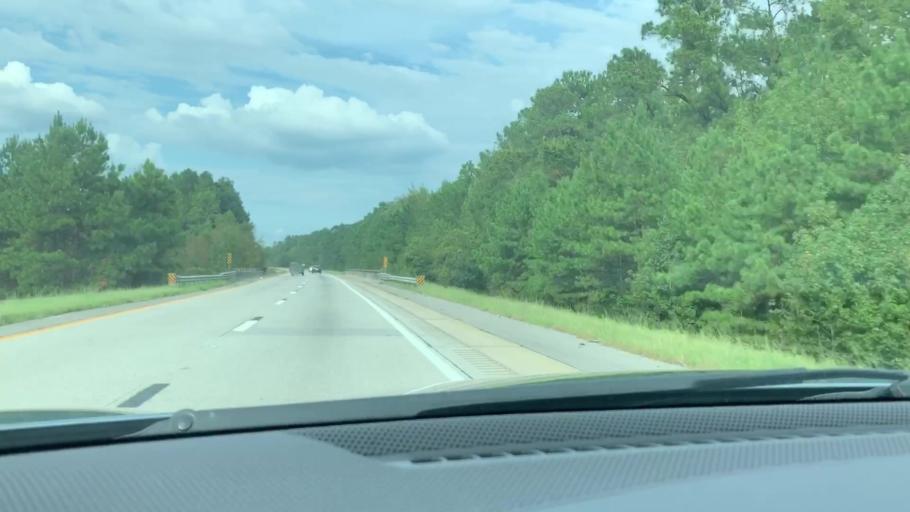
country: US
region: South Carolina
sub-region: Dorchester County
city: Saint George
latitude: 33.0975
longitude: -80.6454
